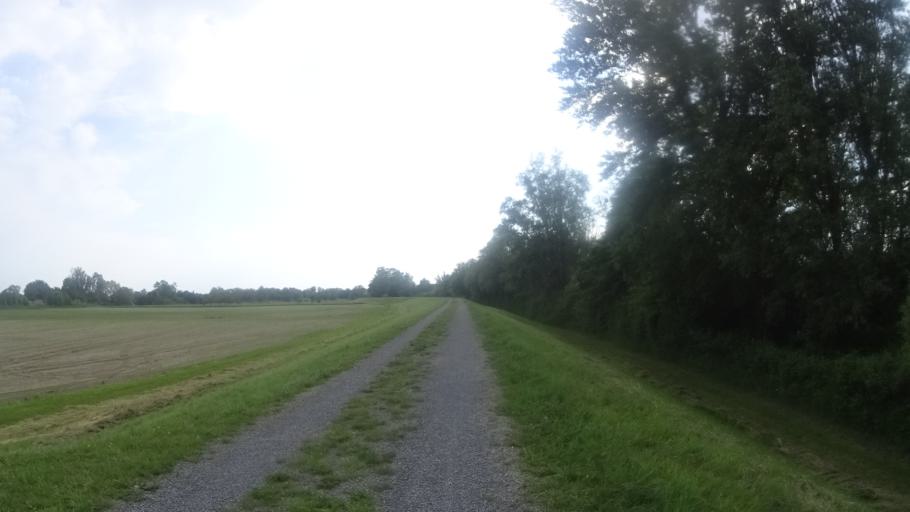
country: DE
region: Baden-Wuerttemberg
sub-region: Karlsruhe Region
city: Hugelsheim
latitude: 48.8016
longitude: 8.0944
